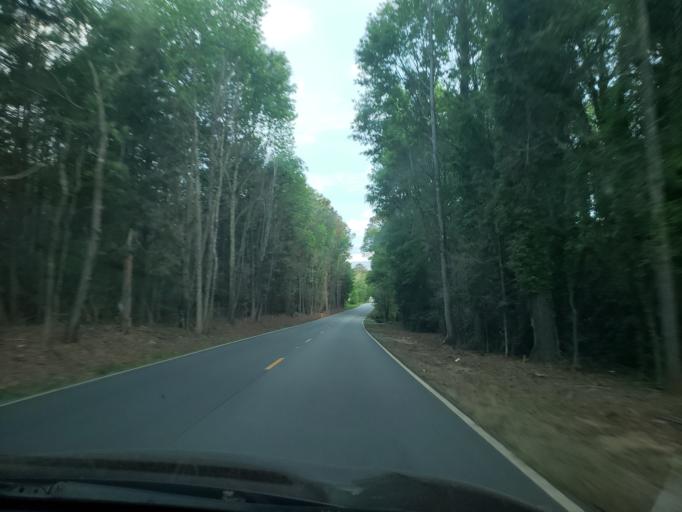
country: US
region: Alabama
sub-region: Tallapoosa County
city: Camp Hill
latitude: 32.6995
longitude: -85.7399
